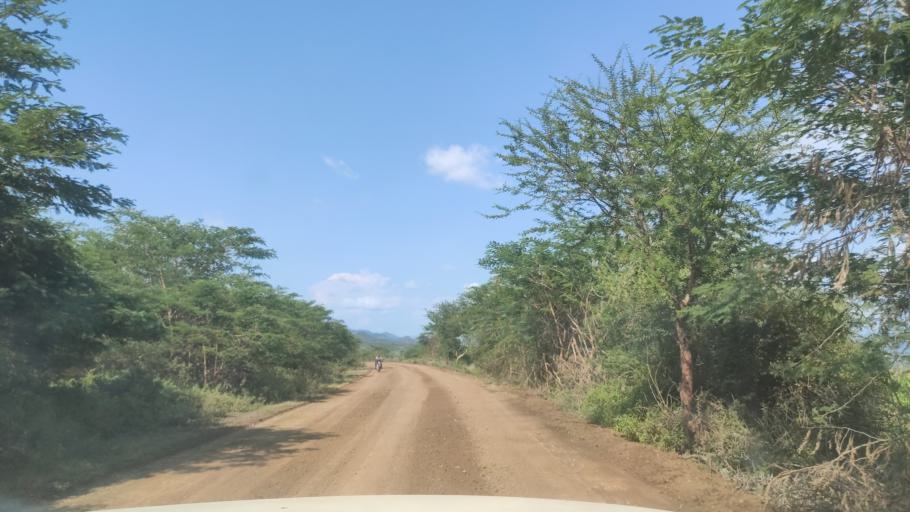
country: ET
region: Southern Nations, Nationalities, and People's Region
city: Felege Neway
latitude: 6.3826
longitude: 37.0937
